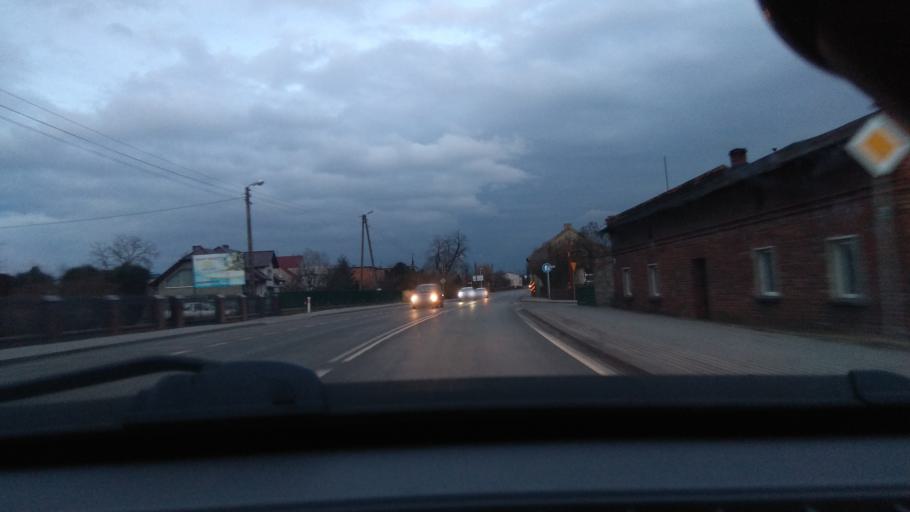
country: PL
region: Greater Poland Voivodeship
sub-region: Powiat kepinski
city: Baranow
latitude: 51.2942
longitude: 18.0349
